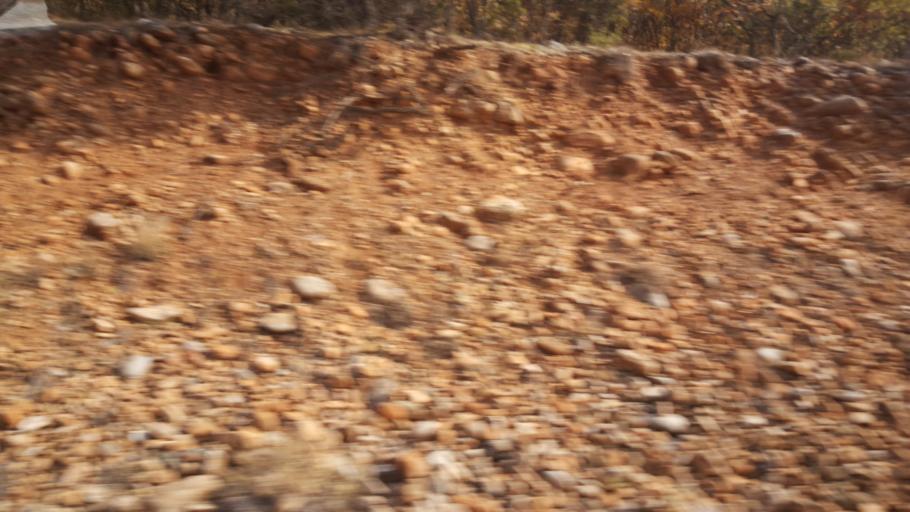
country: TR
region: Eskisehir
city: Mihaliccik
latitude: 39.9643
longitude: 31.3837
